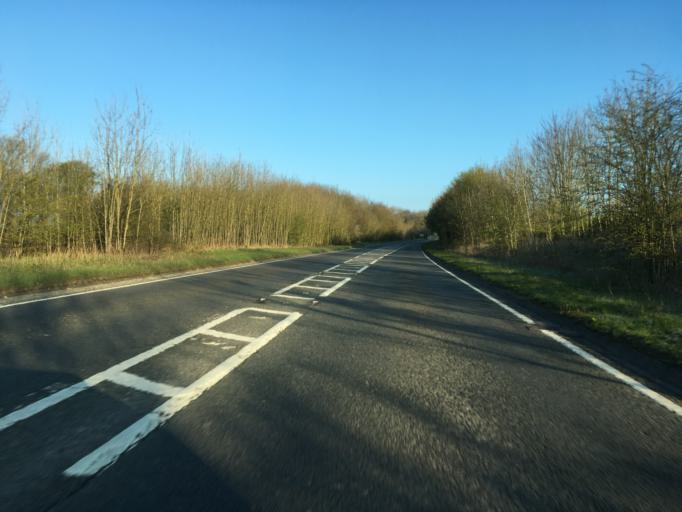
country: GB
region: England
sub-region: Gloucestershire
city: Westfield
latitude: 51.8495
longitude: -1.8875
